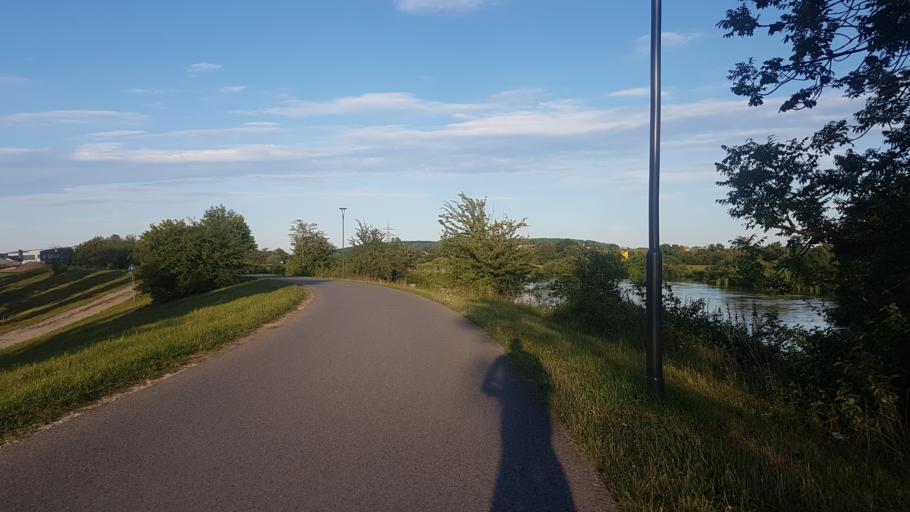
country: DE
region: Bavaria
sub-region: Regierungsbezirk Mittelfranken
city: Gunzenhausen
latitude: 49.1242
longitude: 10.7419
